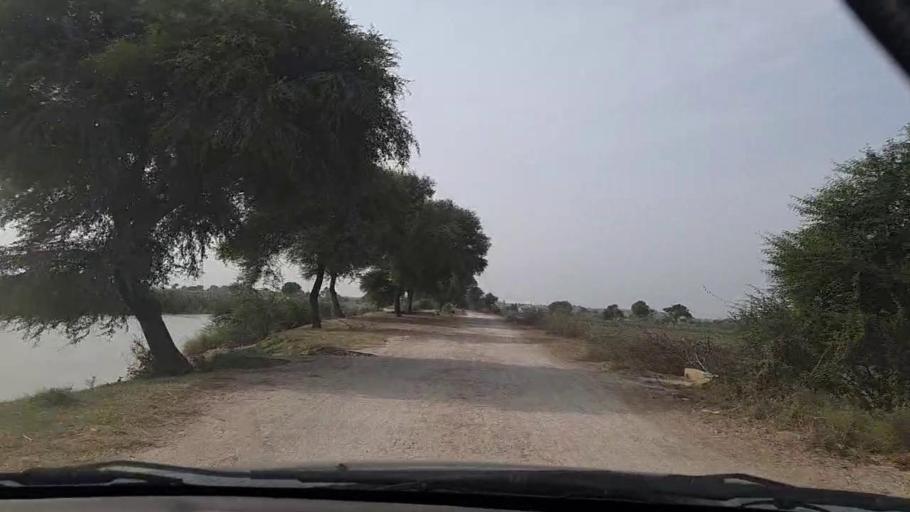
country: PK
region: Sindh
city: Thatta
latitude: 24.5786
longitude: 67.8870
